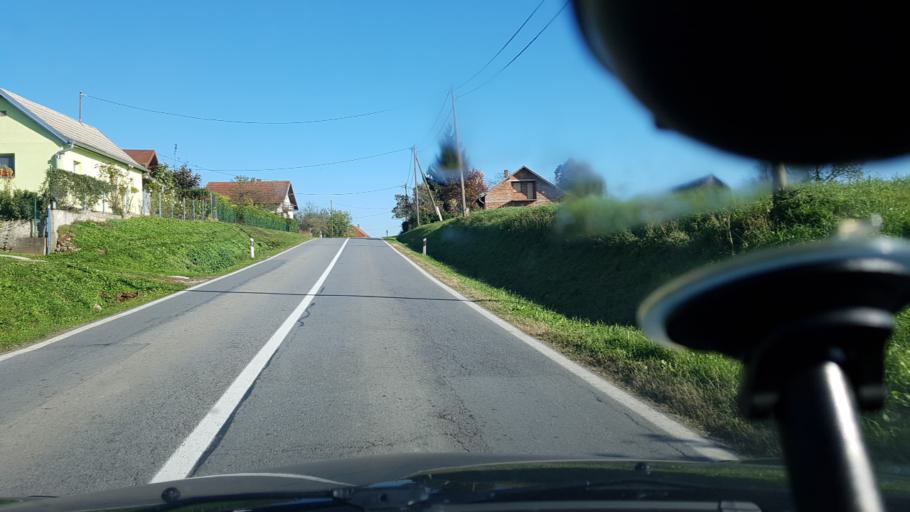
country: HR
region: Bjelovarsko-Bilogorska
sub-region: Grad Cazma
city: Cazma
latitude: 45.7833
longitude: 16.6604
